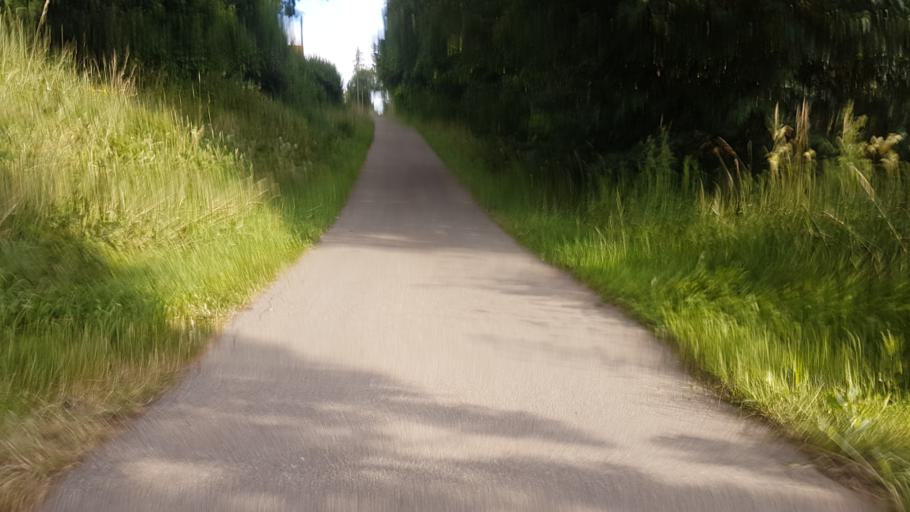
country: DE
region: Baden-Wuerttemberg
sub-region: Freiburg Region
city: Unterkirnach
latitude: 48.0089
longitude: 8.4089
